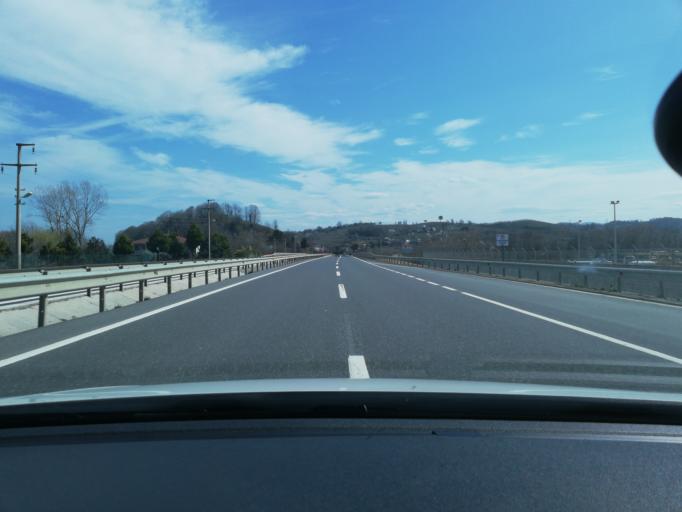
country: TR
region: Duzce
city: Akcakoca
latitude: 41.0966
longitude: 31.2121
